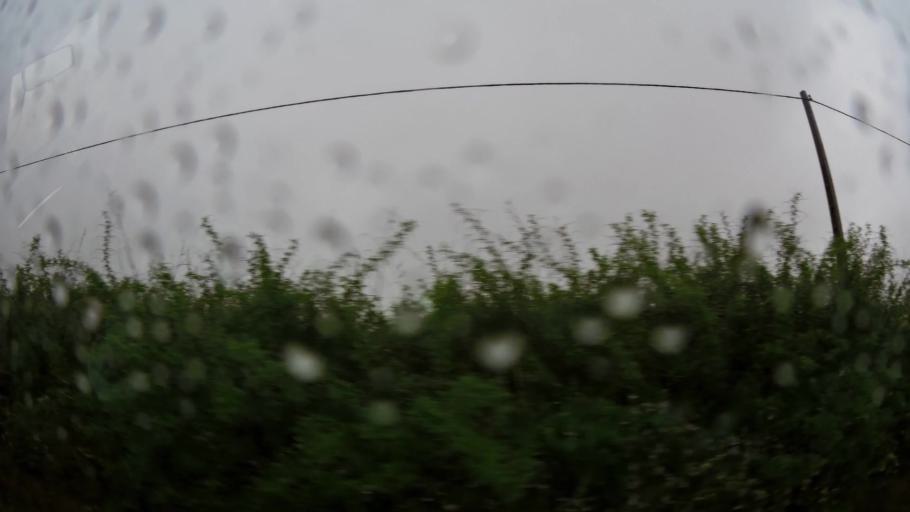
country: MA
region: Oriental
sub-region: Nador
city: Boudinar
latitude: 35.1304
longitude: -3.6470
